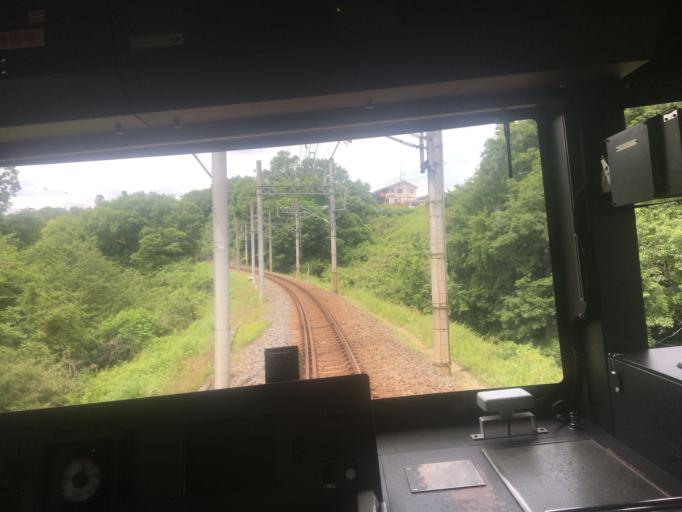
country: JP
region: Saitama
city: Ogawa
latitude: 36.0572
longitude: 139.2954
